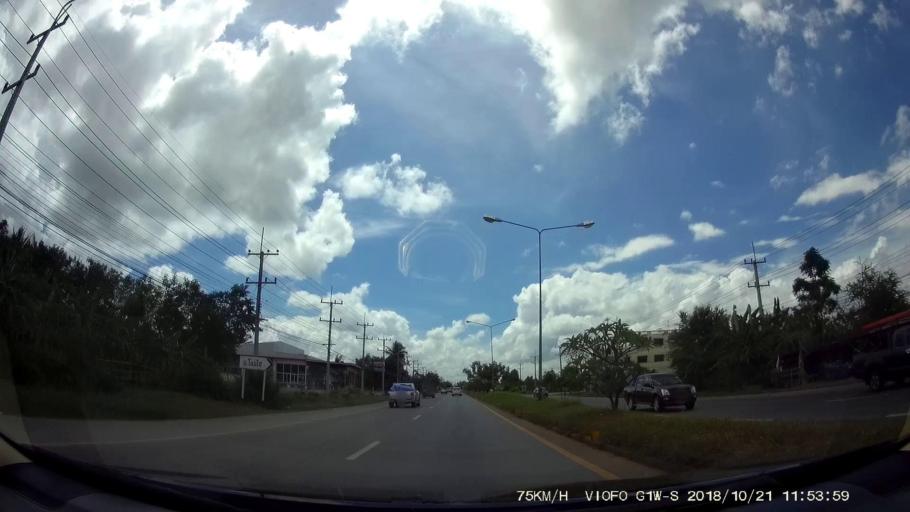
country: TH
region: Chaiyaphum
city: Chatturat
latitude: 15.5896
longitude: 101.9035
